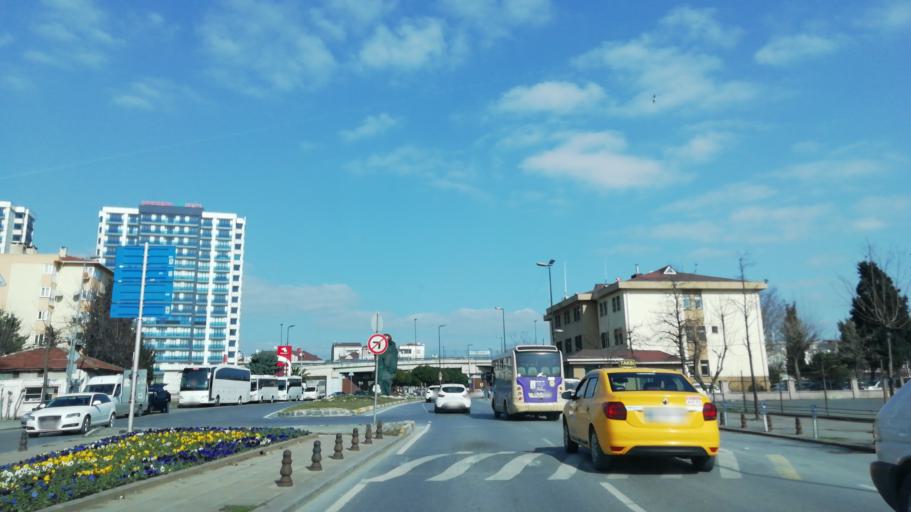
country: TR
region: Istanbul
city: Bahcelievler
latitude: 41.0120
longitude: 28.8472
